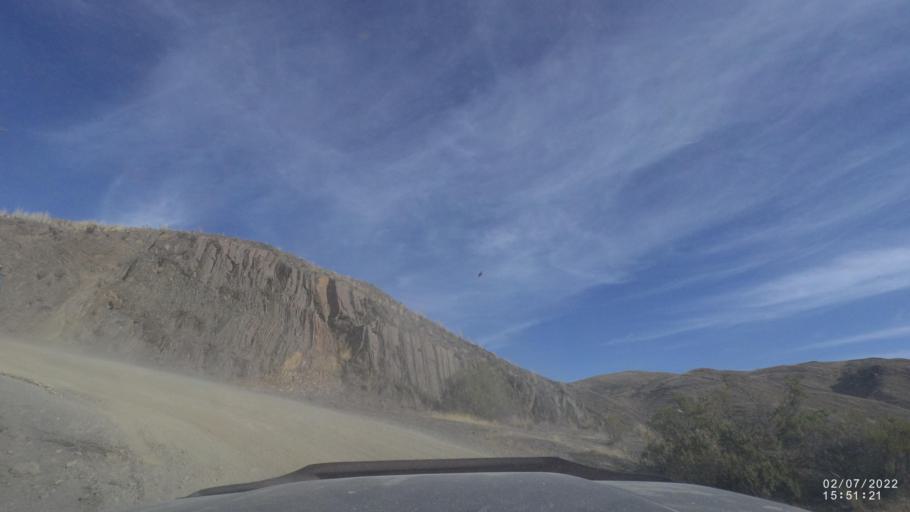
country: BO
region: Cochabamba
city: Irpa Irpa
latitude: -17.9045
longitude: -66.4139
